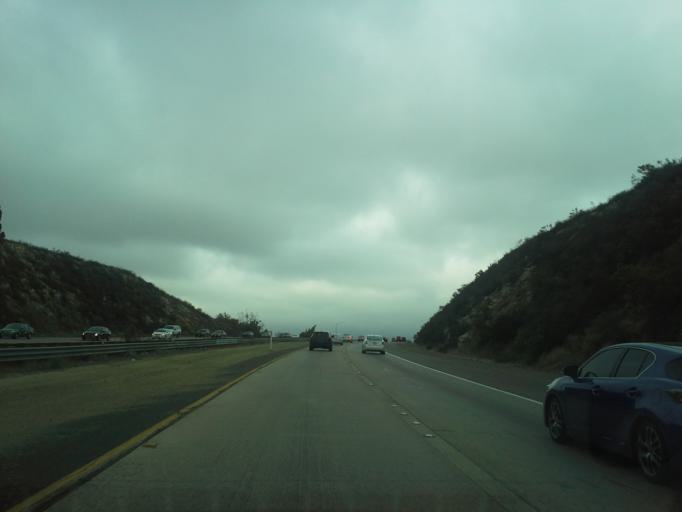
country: US
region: California
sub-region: San Diego County
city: Granite Hills
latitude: 32.8219
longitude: -116.9089
